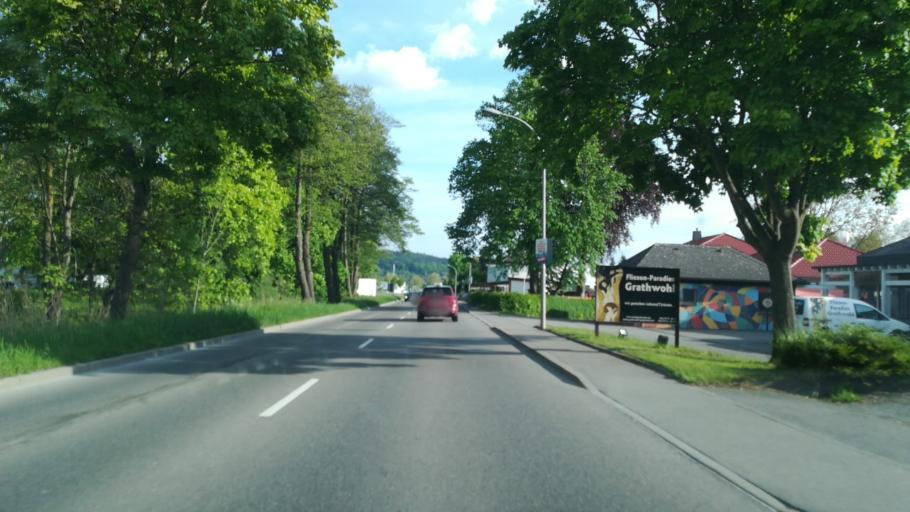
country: DE
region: Baden-Wuerttemberg
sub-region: Freiburg Region
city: Stockach
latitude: 47.8564
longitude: 9.0052
